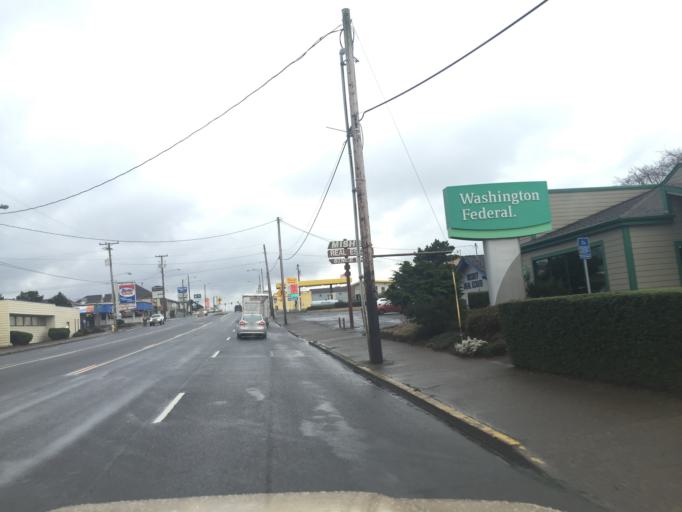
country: US
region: Oregon
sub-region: Lincoln County
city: Newport
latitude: 44.6398
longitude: -124.0532
